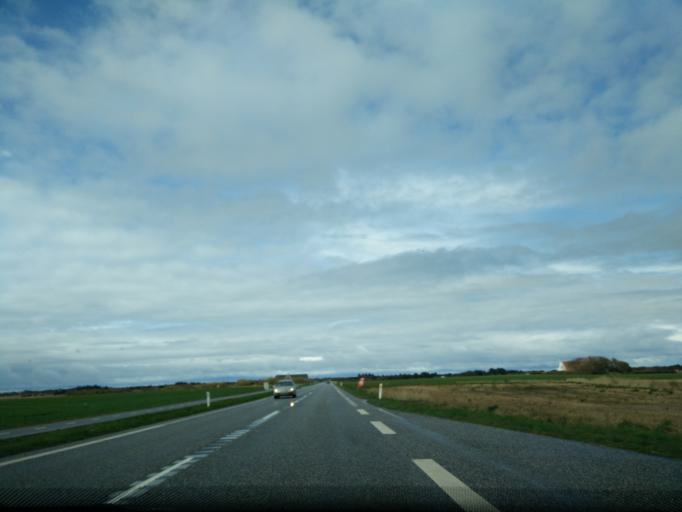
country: DK
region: Central Jutland
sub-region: Ringkobing-Skjern Kommune
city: Ringkobing
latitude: 56.1218
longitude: 8.1509
